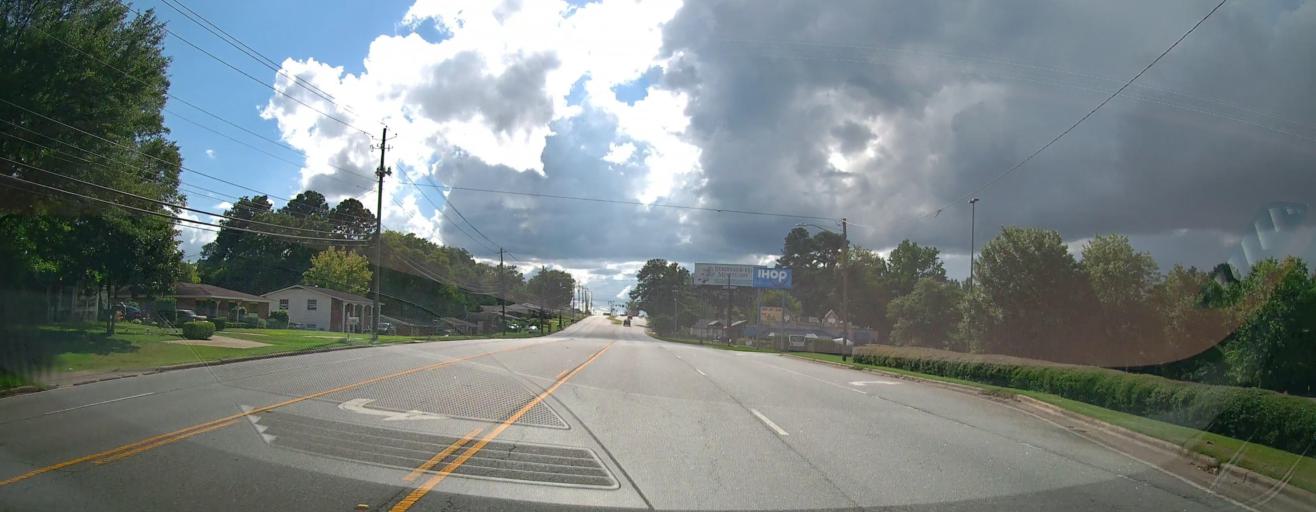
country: US
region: Alabama
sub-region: Russell County
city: Phenix City
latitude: 32.5206
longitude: -84.9603
